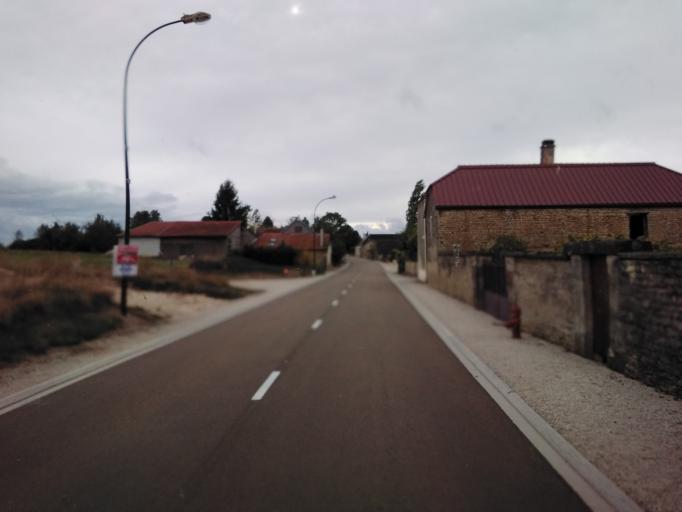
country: FR
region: Champagne-Ardenne
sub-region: Departement de l'Aube
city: Bar-sur-Seine
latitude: 48.1708
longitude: 4.4250
